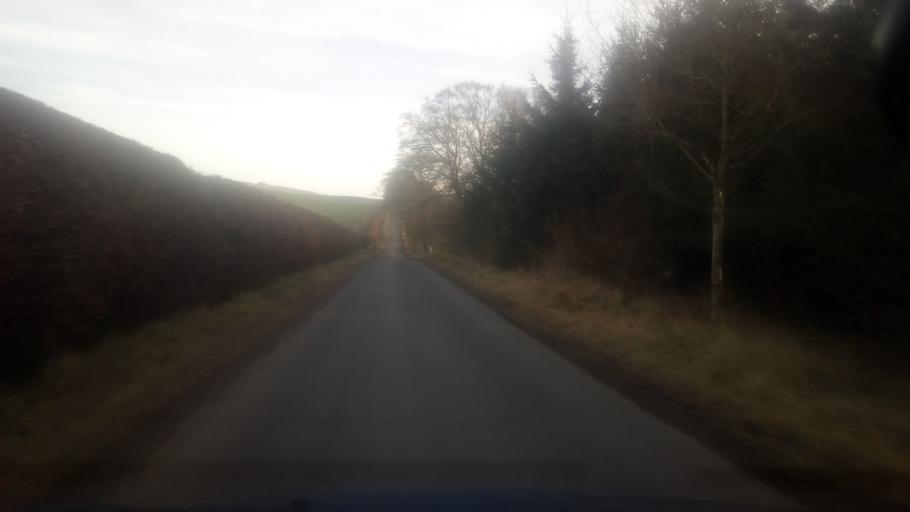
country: GB
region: Scotland
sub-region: The Scottish Borders
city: Jedburgh
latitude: 55.4143
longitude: -2.6166
